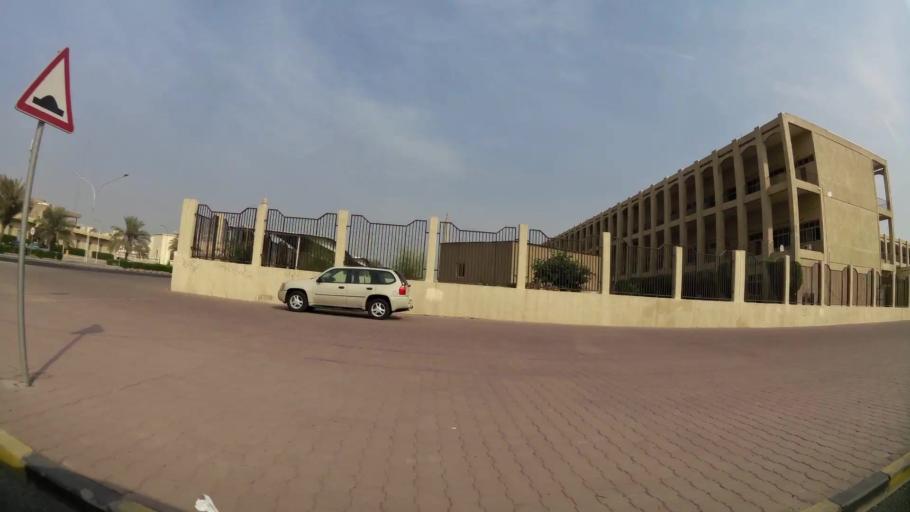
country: KW
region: Al Farwaniyah
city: Al Farwaniyah
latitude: 29.2929
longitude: 47.9542
